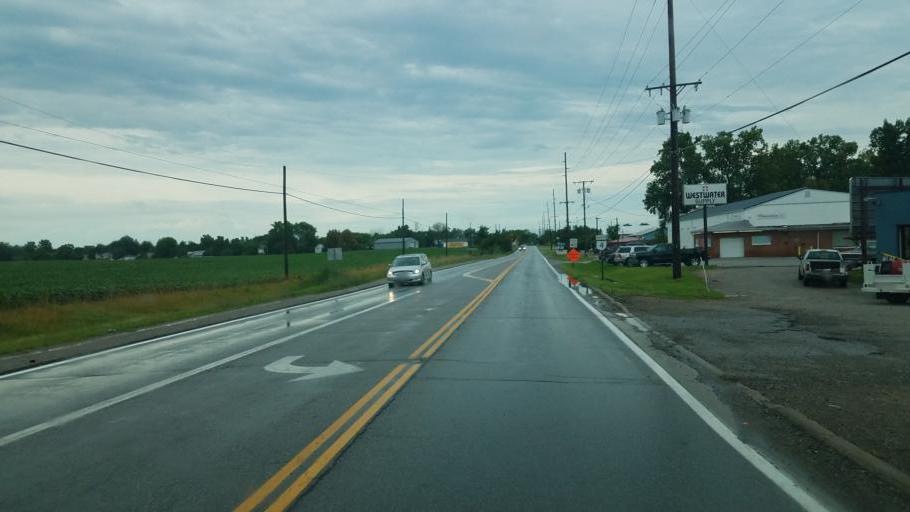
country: US
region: Ohio
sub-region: Marion County
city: Marion
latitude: 40.5638
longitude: -83.1392
